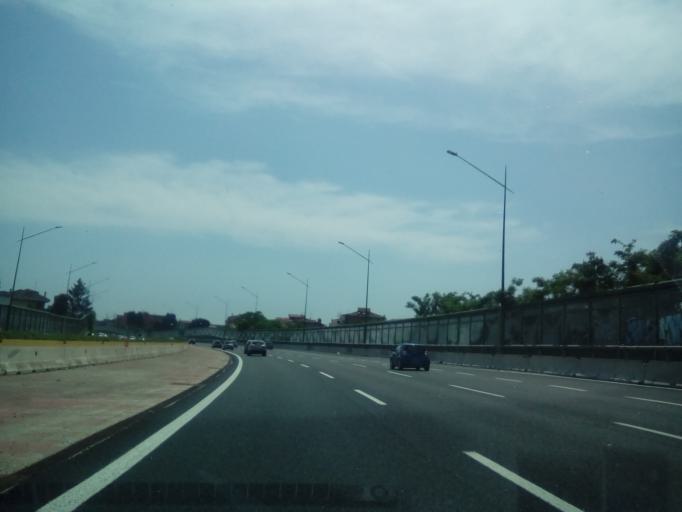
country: IT
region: Latium
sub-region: Citta metropolitana di Roma Capitale
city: Valle Santa
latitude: 41.9562
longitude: 12.3843
